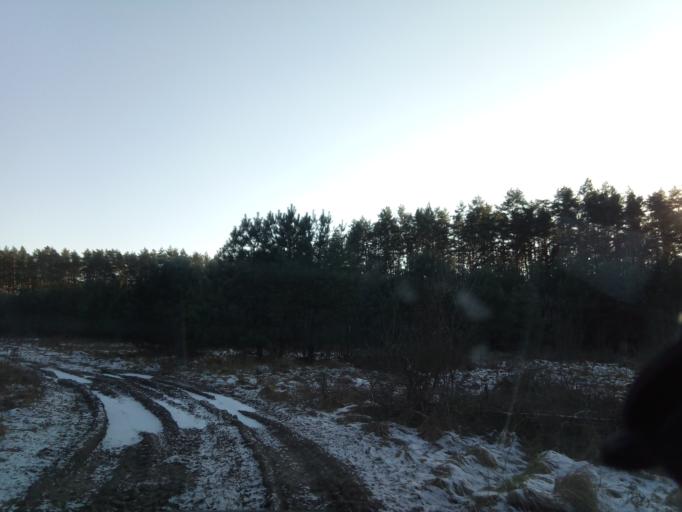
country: LT
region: Alytaus apskritis
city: Druskininkai
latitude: 53.9478
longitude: 23.8763
